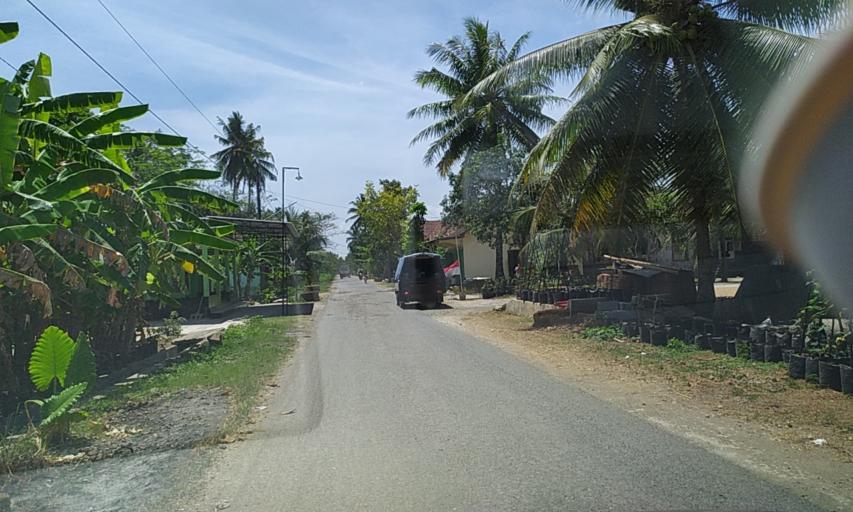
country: ID
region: Central Java
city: Sidaurip
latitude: -7.5575
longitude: 108.7564
